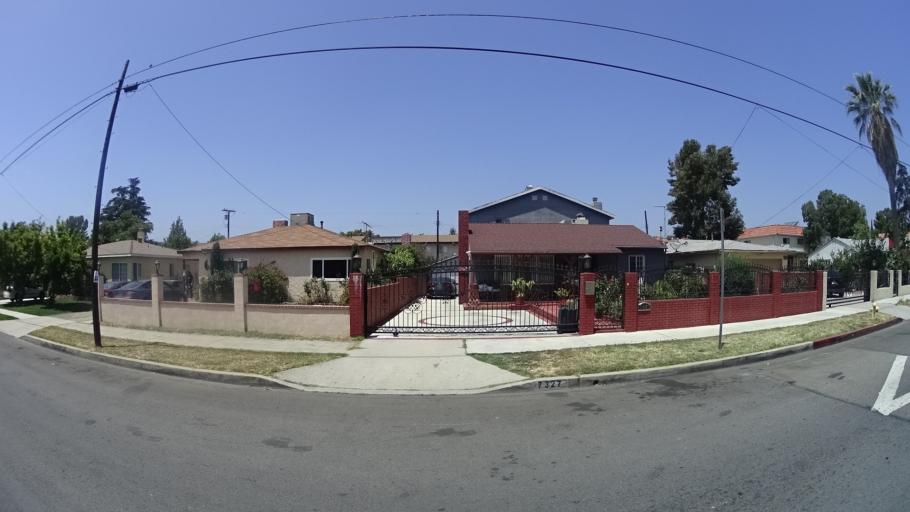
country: US
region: California
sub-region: Los Angeles County
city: Van Nuys
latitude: 34.2038
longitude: -118.4445
